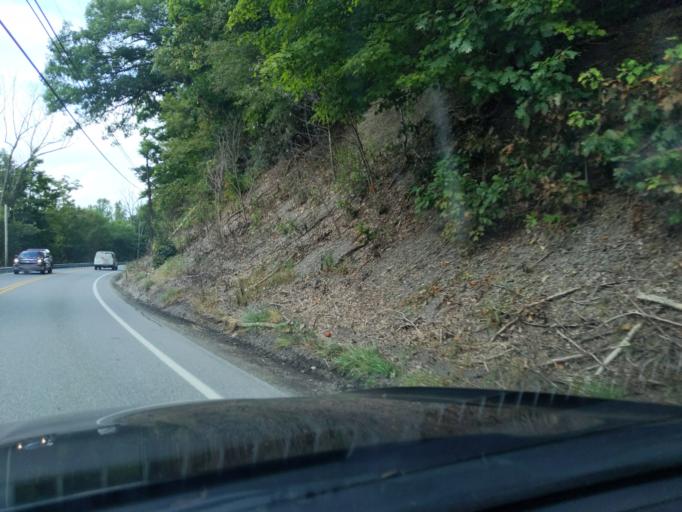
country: US
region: Pennsylvania
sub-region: Blair County
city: Duncansville
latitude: 40.3827
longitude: -78.4145
